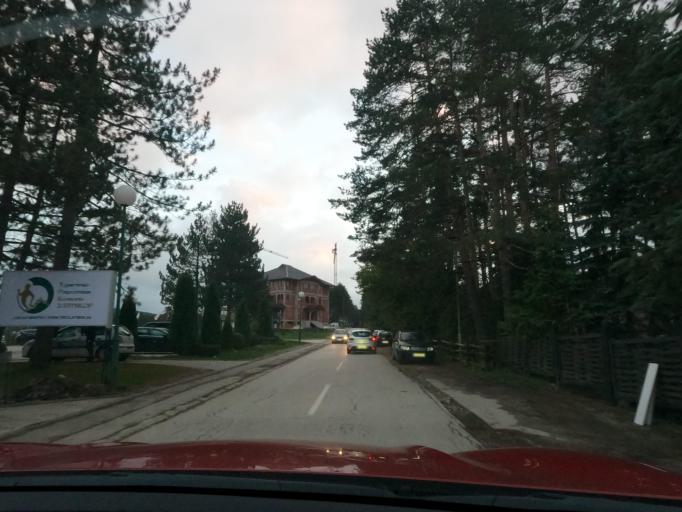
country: RS
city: Zlatibor
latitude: 43.7253
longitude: 19.7041
